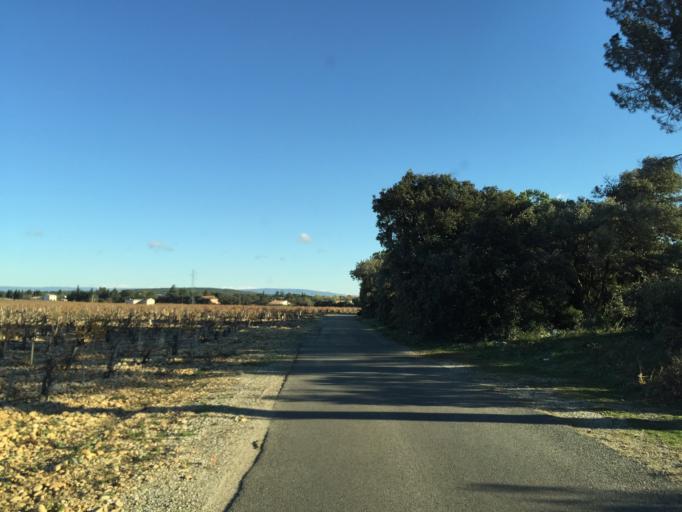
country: FR
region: Provence-Alpes-Cote d'Azur
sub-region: Departement du Vaucluse
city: Sorgues
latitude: 44.0288
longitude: 4.8495
